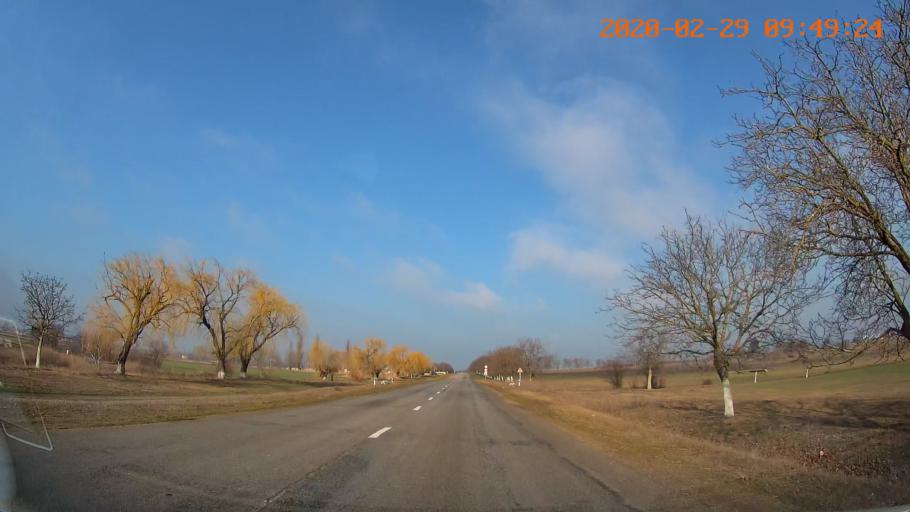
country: MD
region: Telenesti
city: Crasnoe
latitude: 46.6968
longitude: 29.7727
